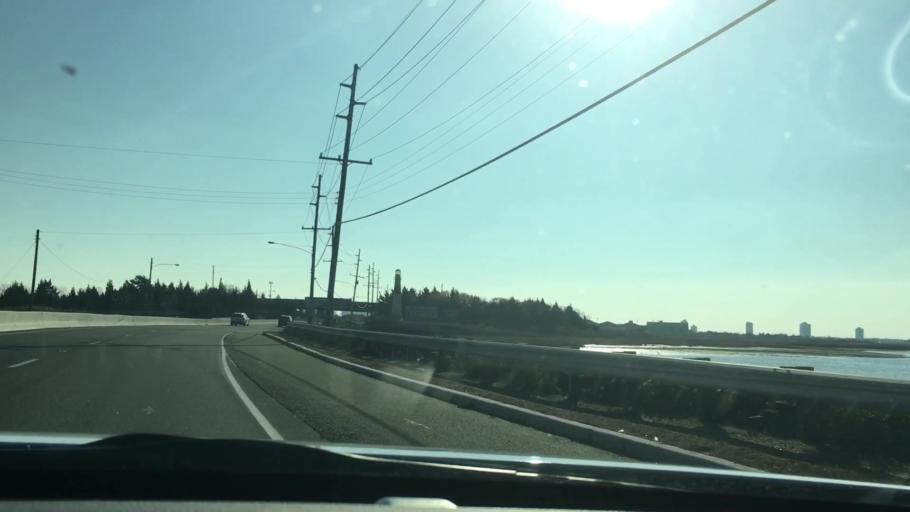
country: US
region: New Jersey
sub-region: Atlantic County
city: Ventnor City
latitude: 39.3764
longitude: -74.4852
